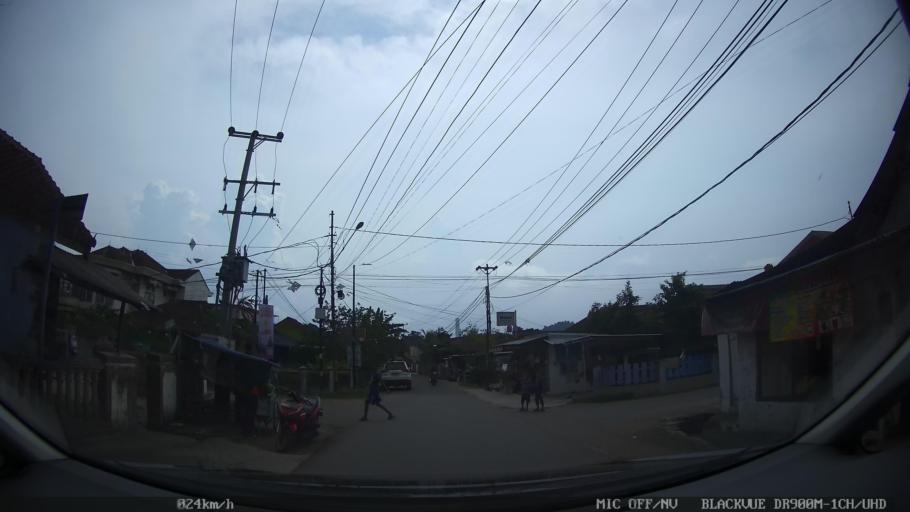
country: ID
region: Lampung
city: Bandarlampung
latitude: -5.4214
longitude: 105.2785
